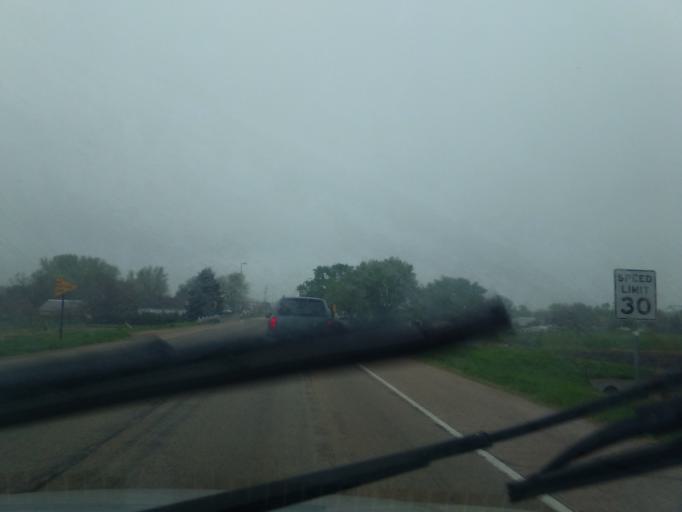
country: US
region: Nebraska
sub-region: Wayne County
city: Wayne
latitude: 42.2234
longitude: -97.0178
